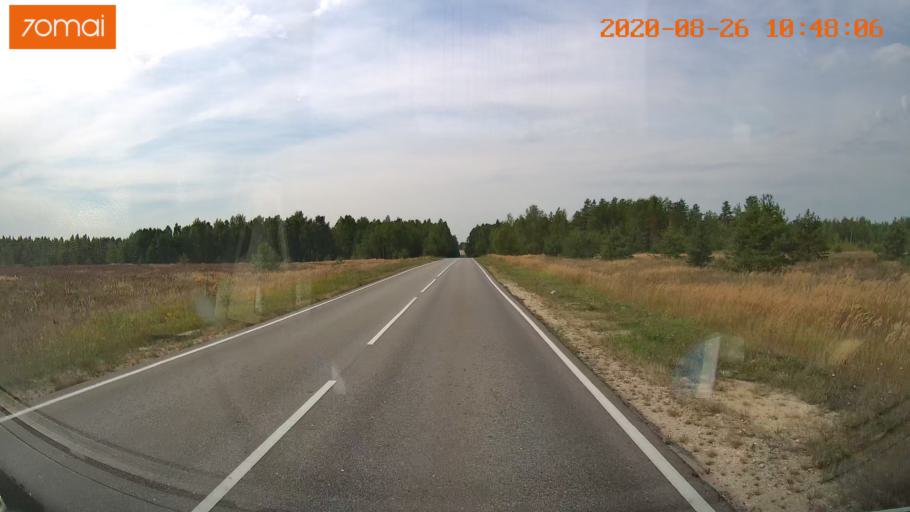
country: RU
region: Rjazan
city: Lashma
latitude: 54.7188
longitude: 41.1791
